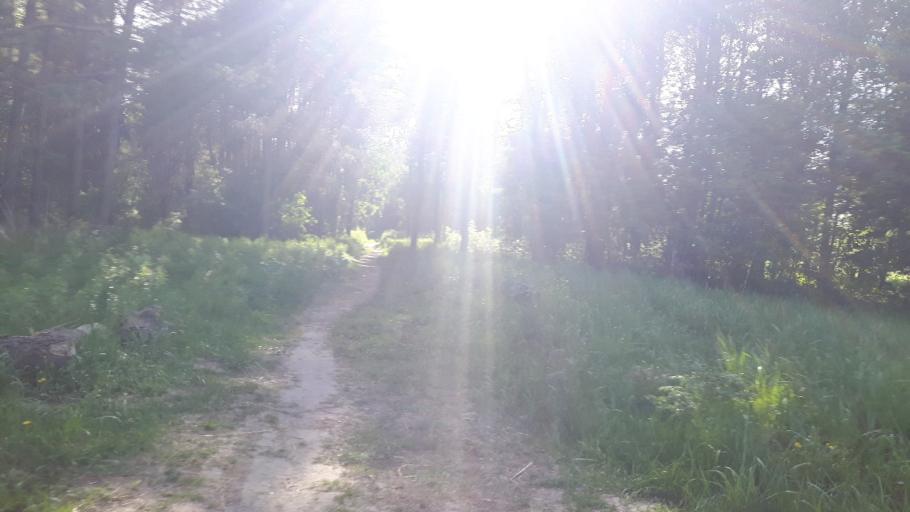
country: EE
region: Harju
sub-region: Tallinna linn
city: Kose
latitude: 59.4488
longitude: 24.9037
